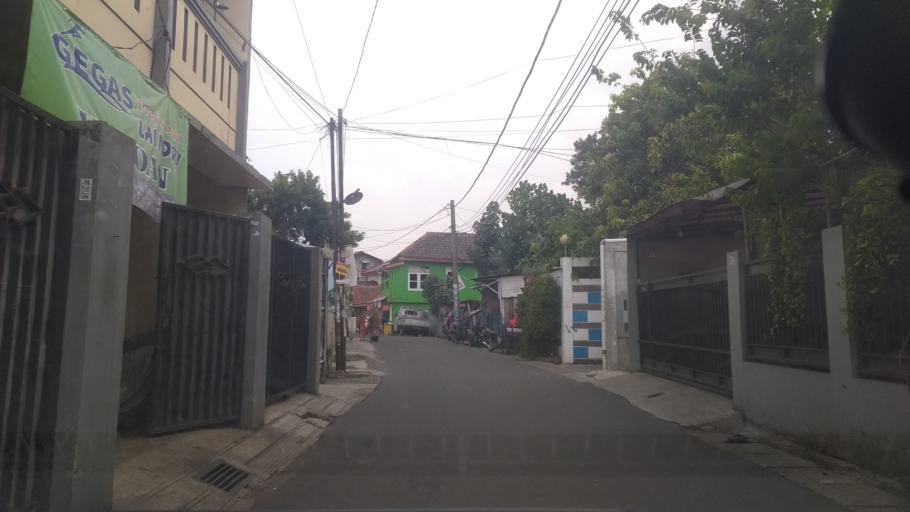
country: ID
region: Banten
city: South Tangerang
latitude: -6.2623
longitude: 106.7389
